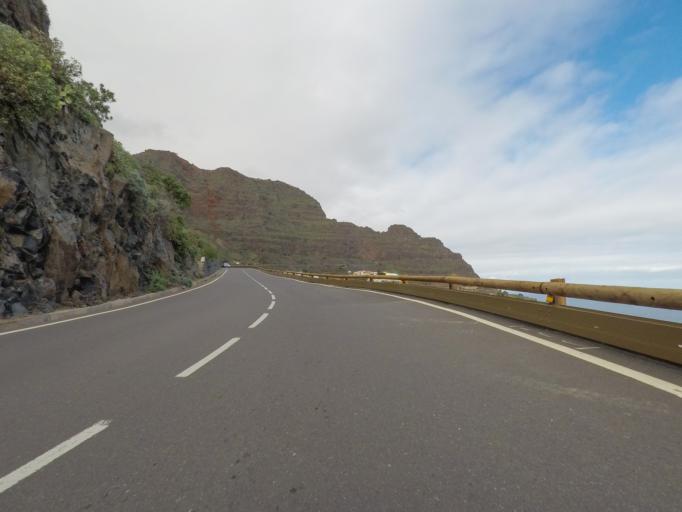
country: ES
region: Canary Islands
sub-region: Provincia de Santa Cruz de Tenerife
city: Agulo
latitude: 28.1850
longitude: -17.1885
